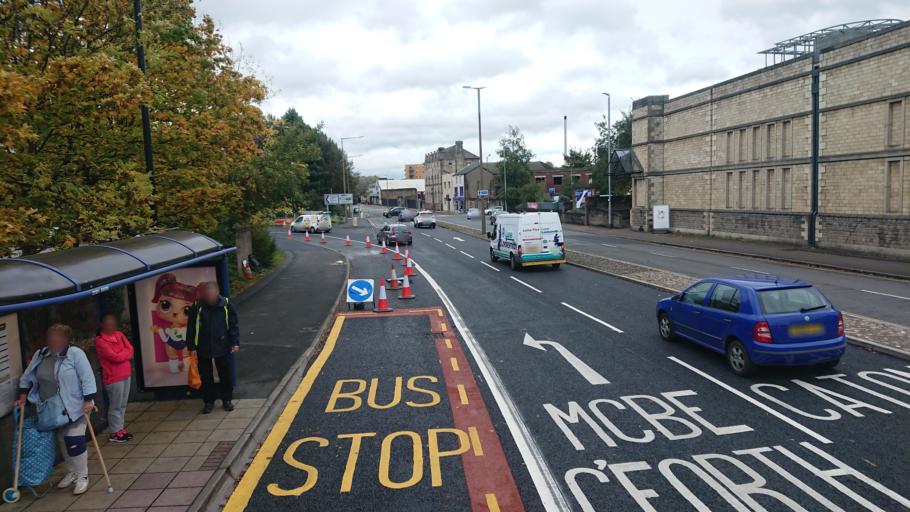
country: GB
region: England
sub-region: Lancashire
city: Lancaster
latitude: 54.0517
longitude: -2.7973
